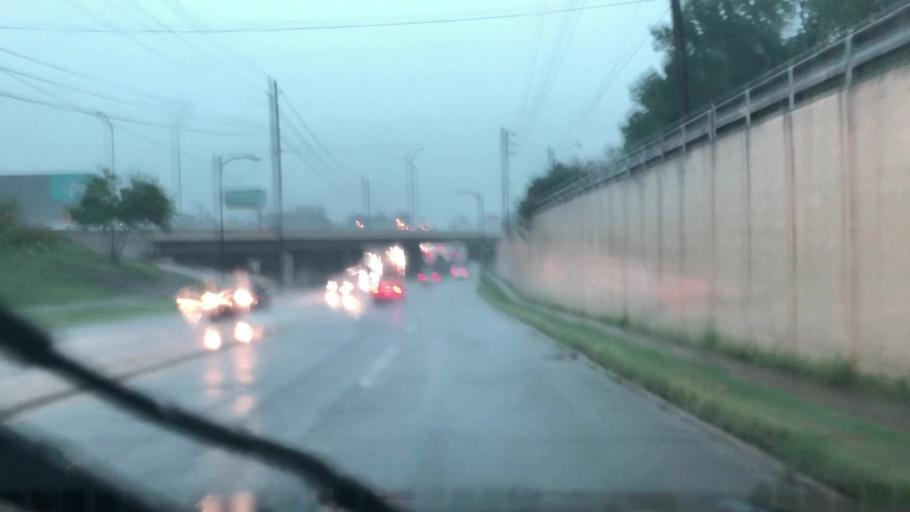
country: US
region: Oklahoma
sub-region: Tulsa County
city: Tulsa
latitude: 36.1189
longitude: -95.9194
